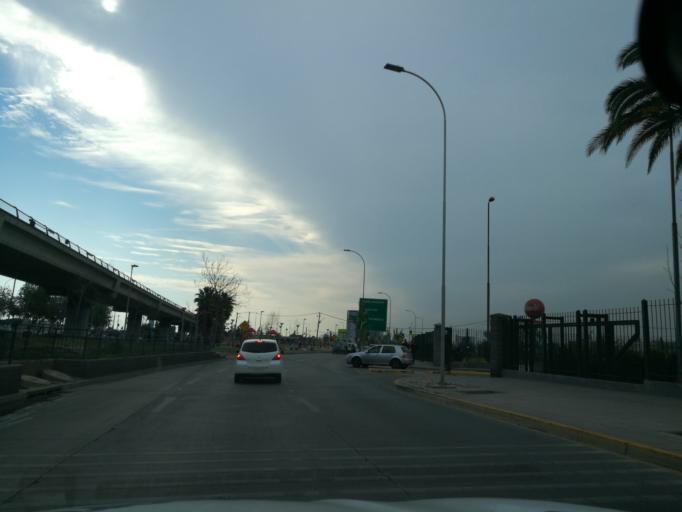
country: CL
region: Santiago Metropolitan
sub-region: Provincia de Santiago
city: Villa Presidente Frei, Nunoa, Santiago, Chile
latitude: -33.5100
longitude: -70.6095
